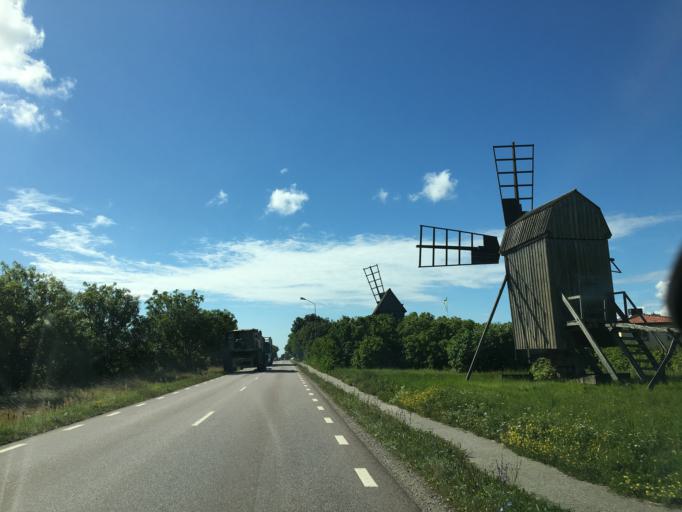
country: SE
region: Kalmar
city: Faerjestaden
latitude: 56.5813
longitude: 16.4617
